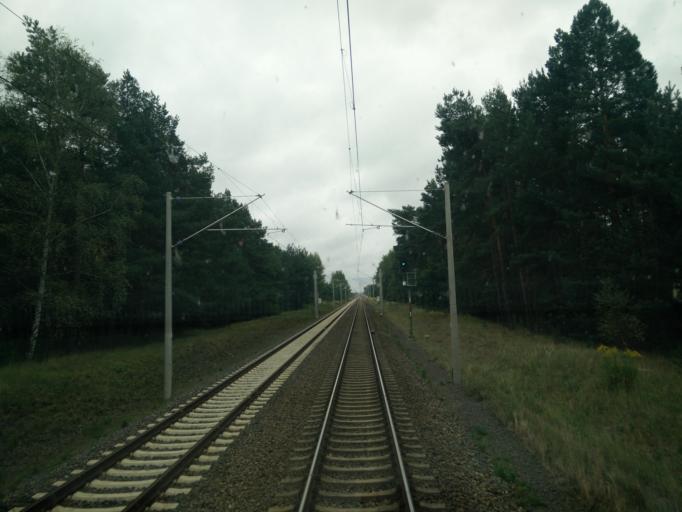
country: DE
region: Brandenburg
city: Kasel-Golzig
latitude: 51.9825
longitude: 13.7906
